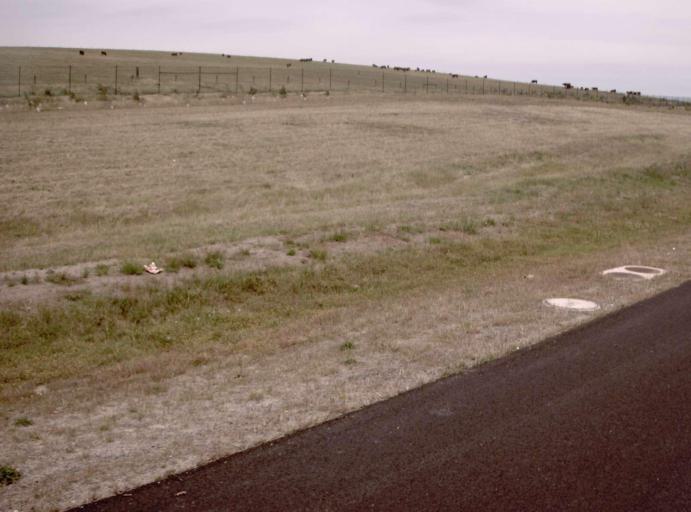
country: AU
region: Victoria
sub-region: Mornington Peninsula
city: Moorooduc
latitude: -38.2691
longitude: 145.0948
